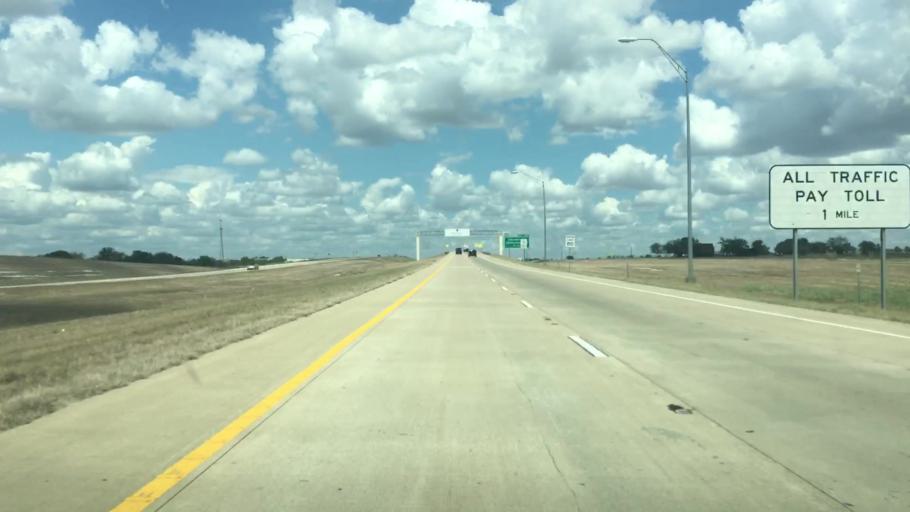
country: US
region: Texas
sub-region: Williamson County
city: Hutto
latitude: 30.5695
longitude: -97.5820
